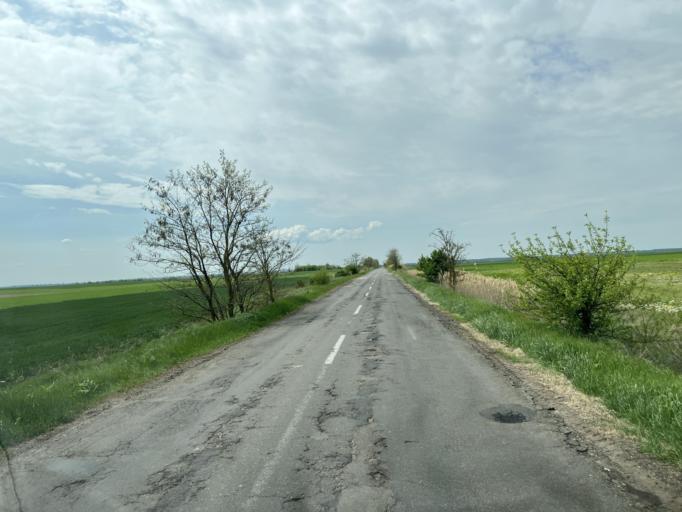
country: HU
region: Pest
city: Abony
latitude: 47.1651
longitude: 19.9769
